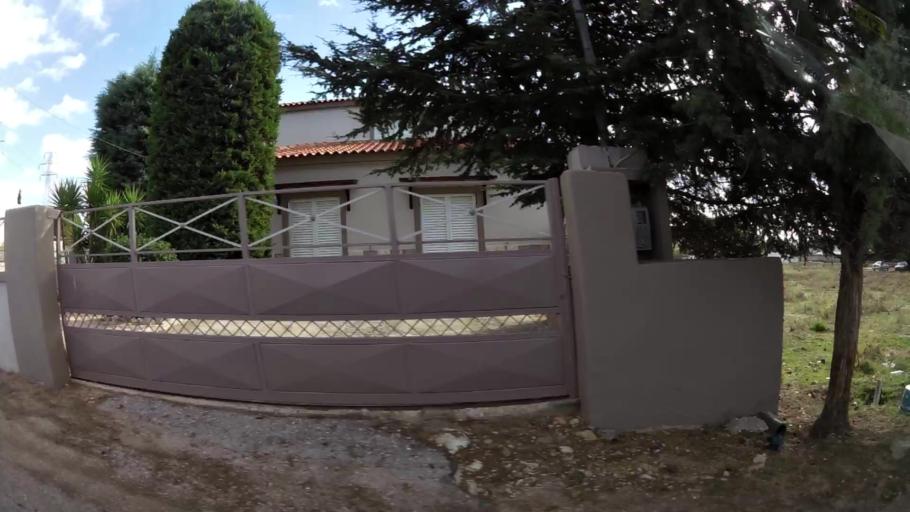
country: GR
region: Attica
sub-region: Nomarchia Anatolikis Attikis
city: Thrakomakedones
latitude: 38.1113
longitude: 23.7571
